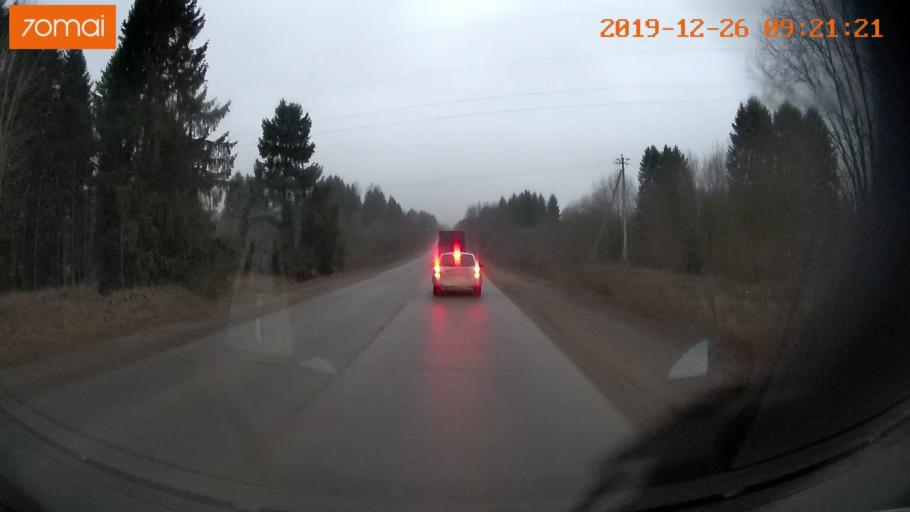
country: RU
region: Vologda
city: Gryazovets
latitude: 58.9697
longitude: 40.2249
